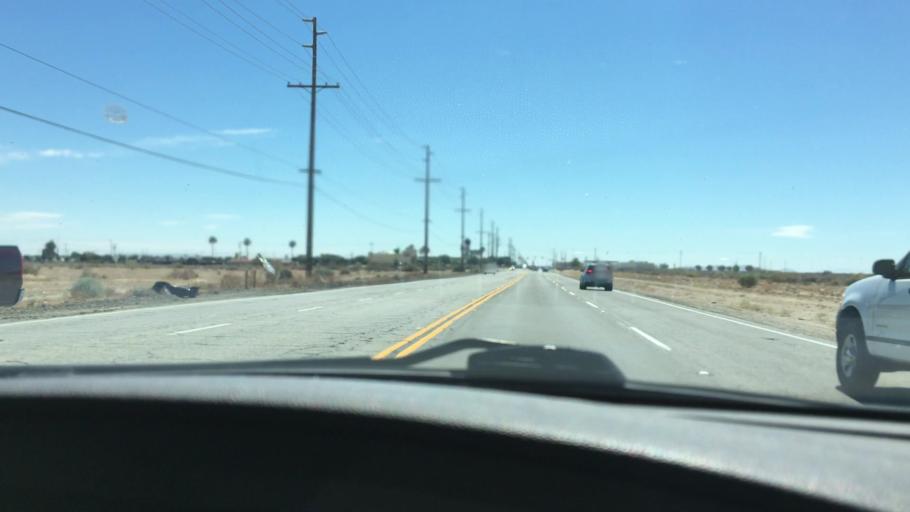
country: US
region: California
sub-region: Los Angeles County
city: Lancaster
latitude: 34.6458
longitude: -118.1344
